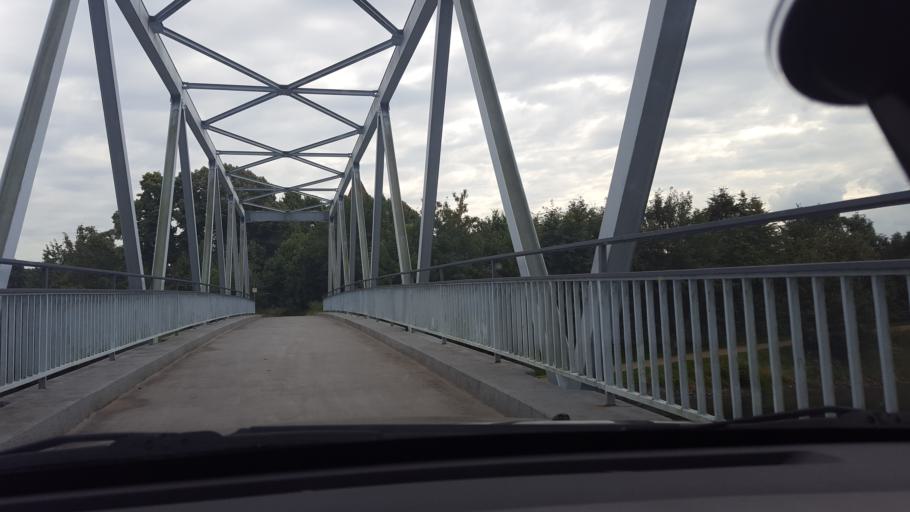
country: DE
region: North Rhine-Westphalia
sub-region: Regierungsbezirk Munster
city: Haltern
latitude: 51.7213
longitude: 7.2339
